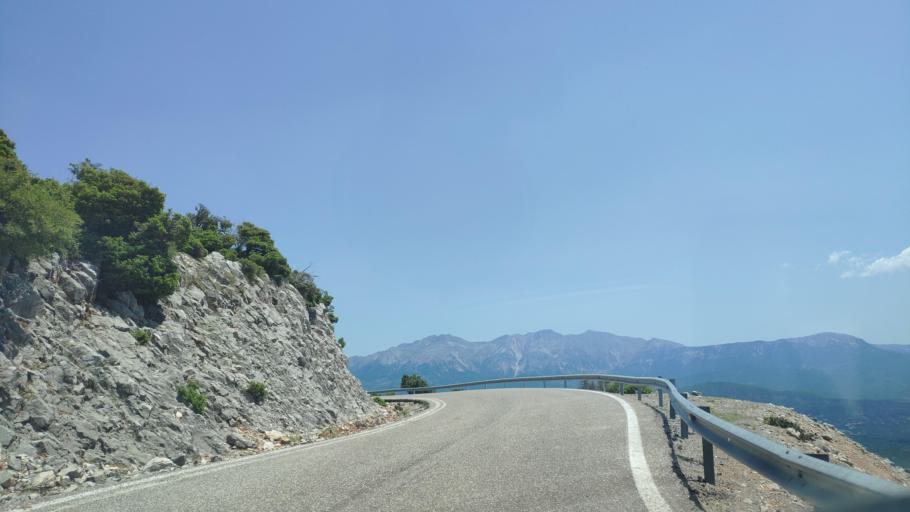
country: GR
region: West Greece
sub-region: Nomos Aitolias kai Akarnanias
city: Krikellos
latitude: 39.0556
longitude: 21.3838
